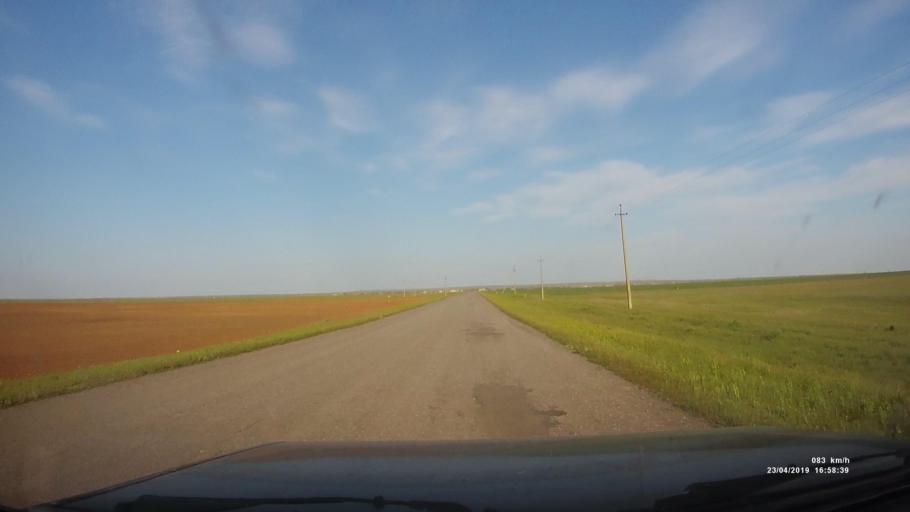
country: RU
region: Kalmykiya
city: Priyutnoye
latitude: 46.3081
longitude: 43.3764
